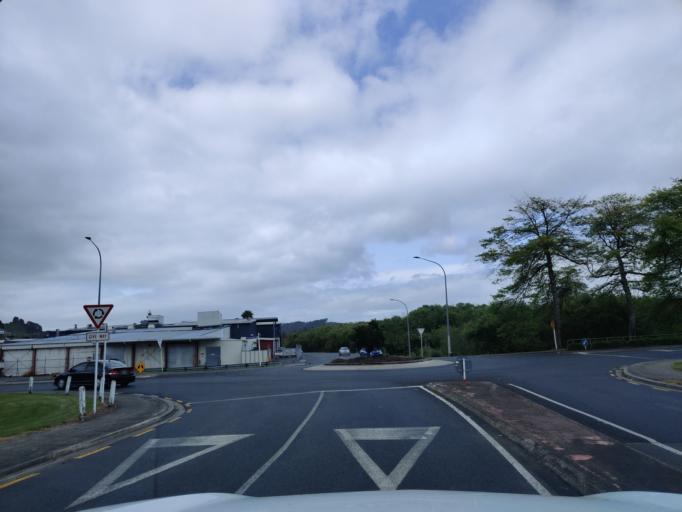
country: NZ
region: Waikato
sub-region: Waikato District
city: Ngaruawahia
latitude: -37.5663
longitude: 175.1579
